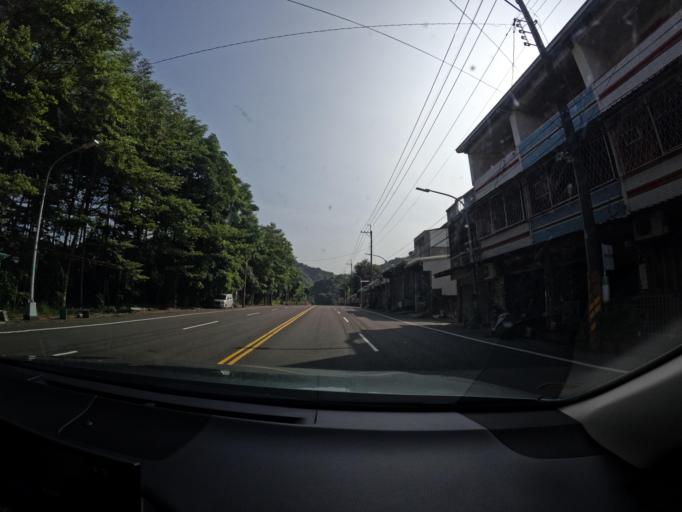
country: TW
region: Taiwan
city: Yujing
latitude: 23.0695
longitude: 120.5154
